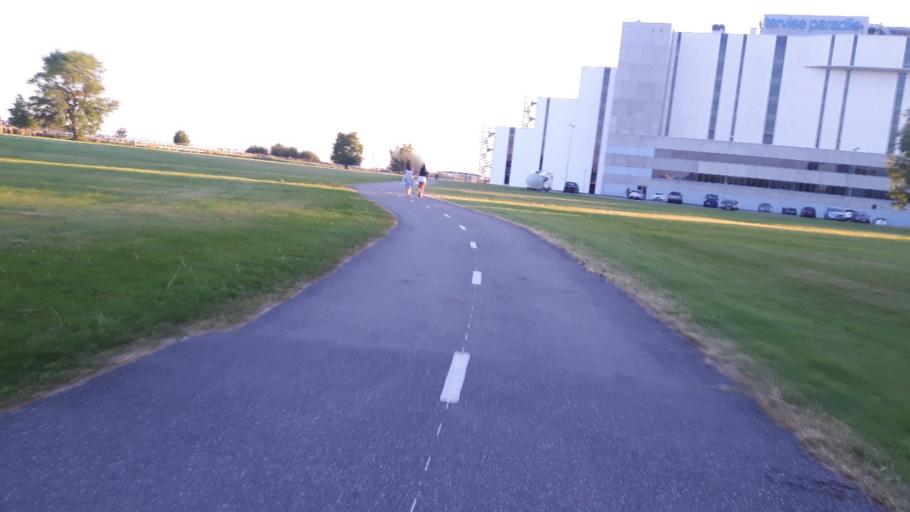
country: EE
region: Paernumaa
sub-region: Paernu linn
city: Parnu
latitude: 58.3731
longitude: 24.5141
